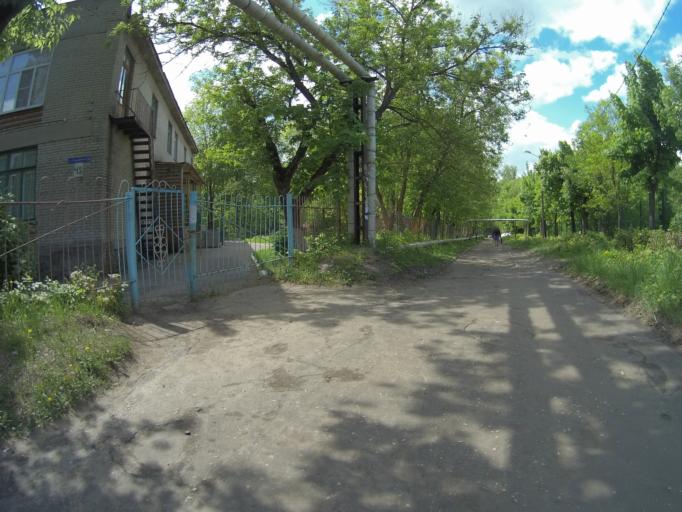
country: RU
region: Vladimir
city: Vladimir
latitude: 56.1342
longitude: 40.3561
